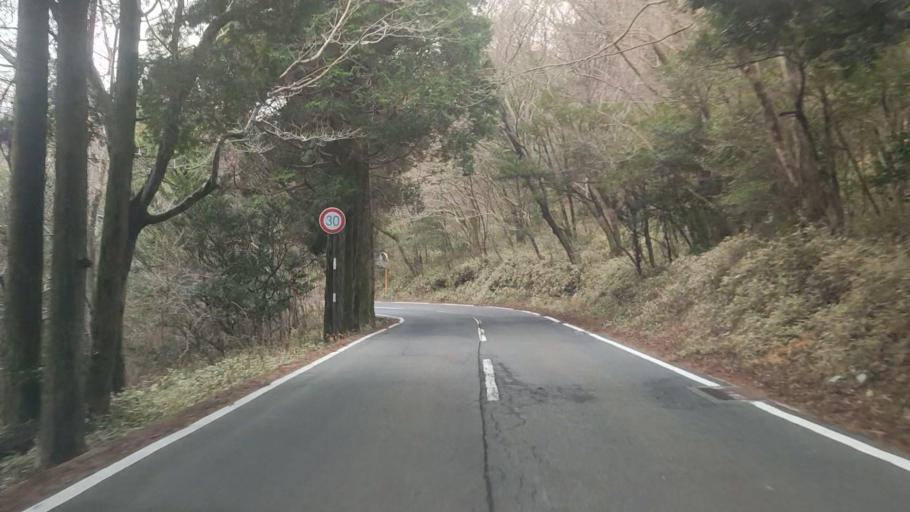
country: JP
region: Nagasaki
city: Shimabara
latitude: 32.7540
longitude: 130.2738
